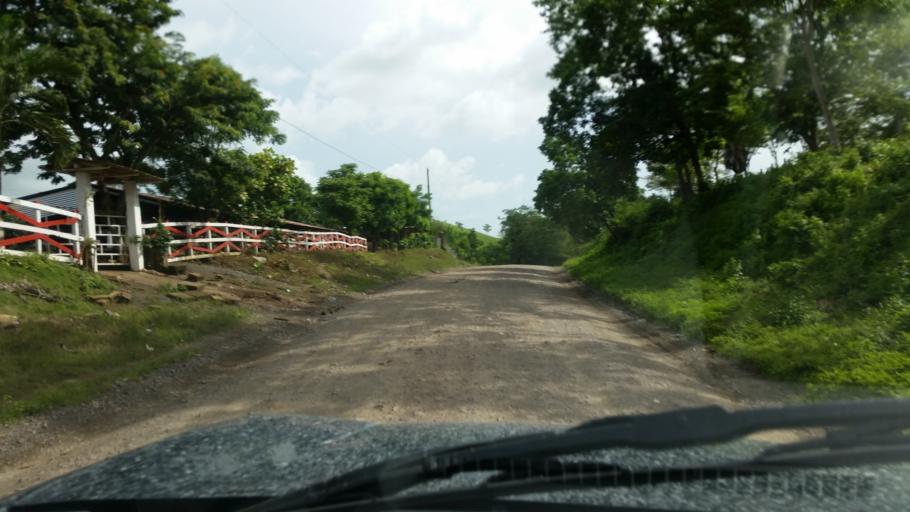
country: NI
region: Atlantico Norte (RAAN)
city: Siuna
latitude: 13.5993
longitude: -84.8015
